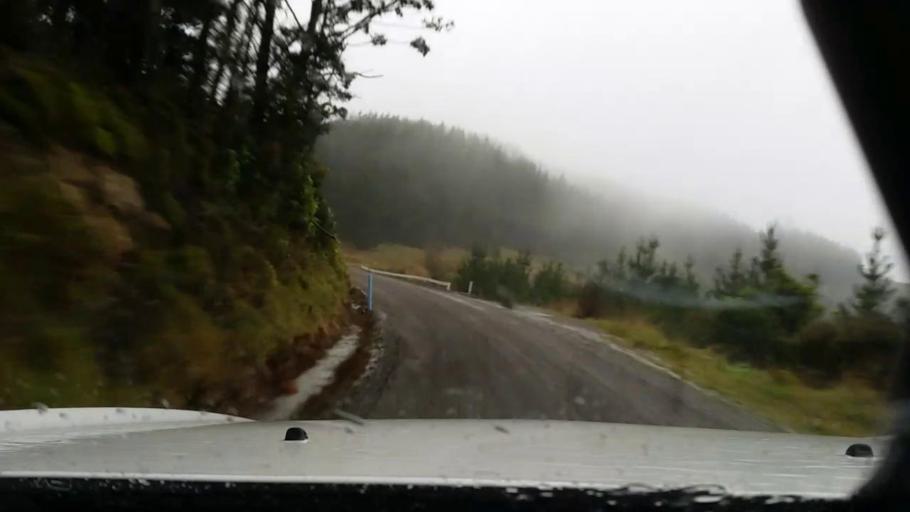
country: NZ
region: Wellington
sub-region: Masterton District
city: Masterton
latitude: -41.1883
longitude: 175.8177
